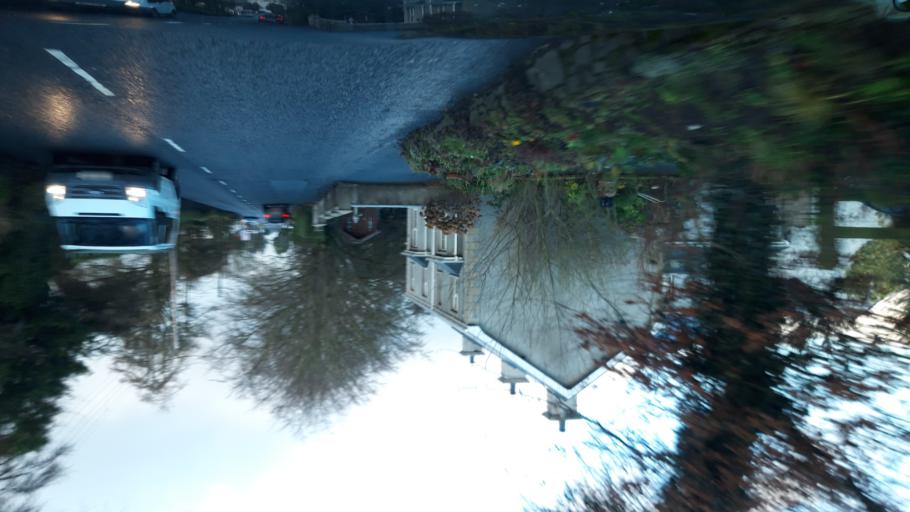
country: GB
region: Northern Ireland
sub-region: Moyle District
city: Ballycastle
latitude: 55.1300
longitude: -6.3259
